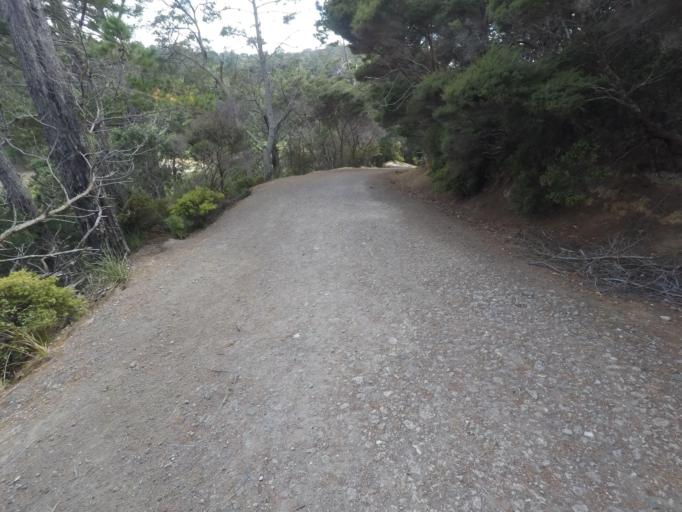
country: NZ
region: Auckland
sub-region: Auckland
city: North Shore
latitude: -36.8144
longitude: 174.6969
